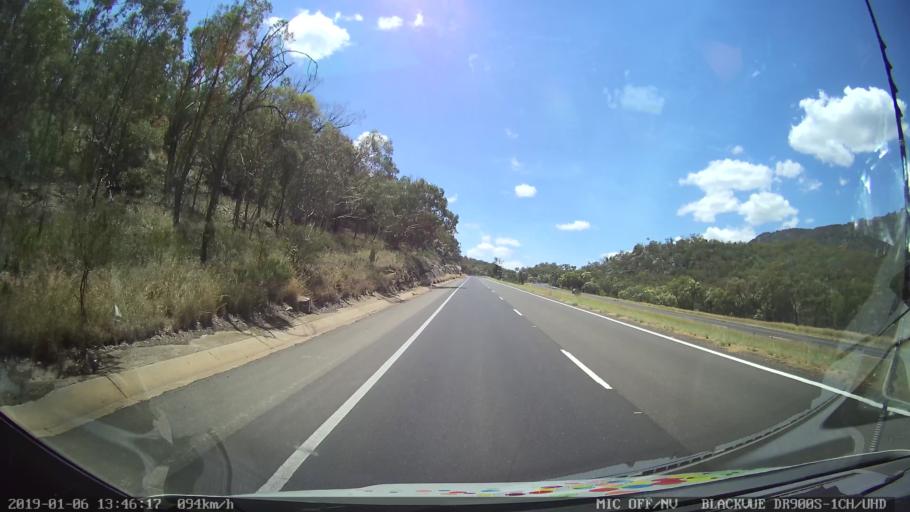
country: AU
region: New South Wales
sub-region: Tamworth Municipality
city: Kootingal
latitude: -30.9798
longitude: 151.1007
